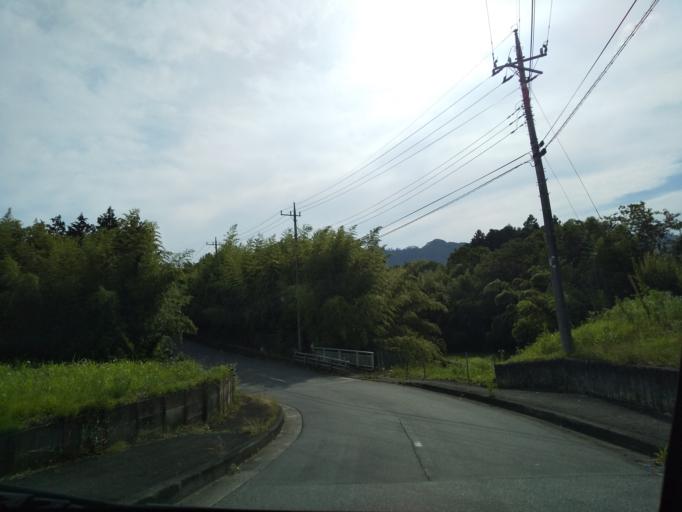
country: JP
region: Kanagawa
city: Atsugi
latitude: 35.4915
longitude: 139.3152
